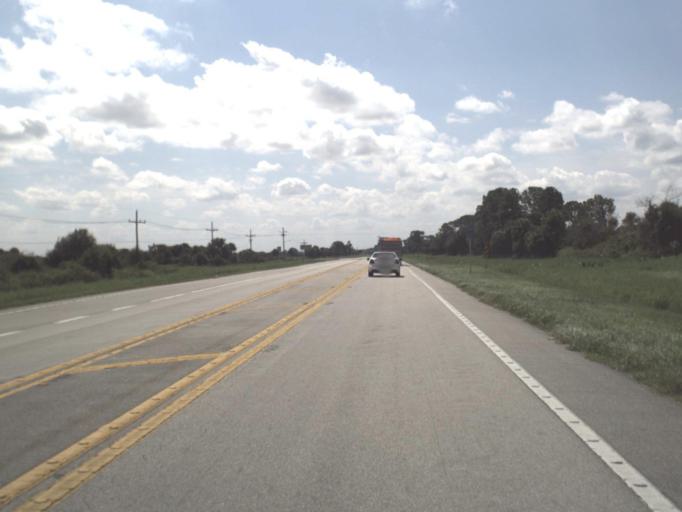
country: US
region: Florida
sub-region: Hendry County
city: Port LaBelle
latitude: 26.5990
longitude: -81.4367
